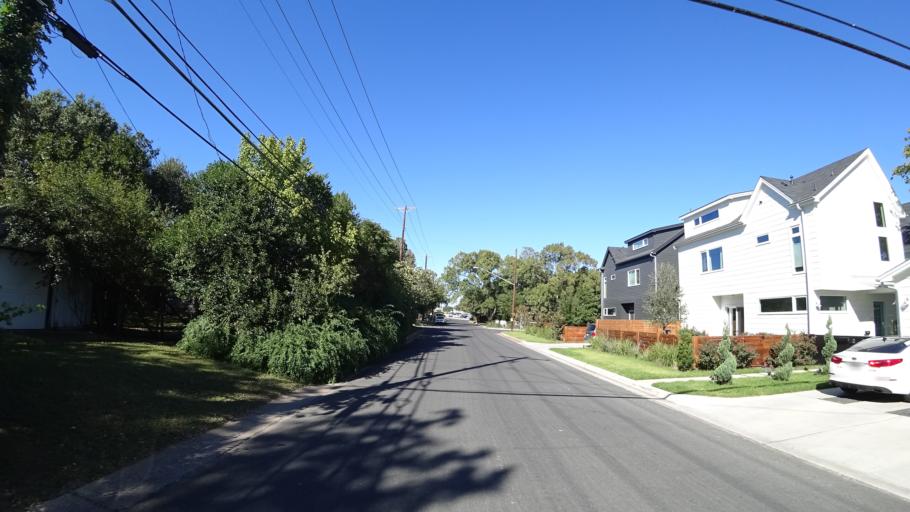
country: US
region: Texas
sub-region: Travis County
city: Austin
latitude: 30.3119
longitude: -97.7536
